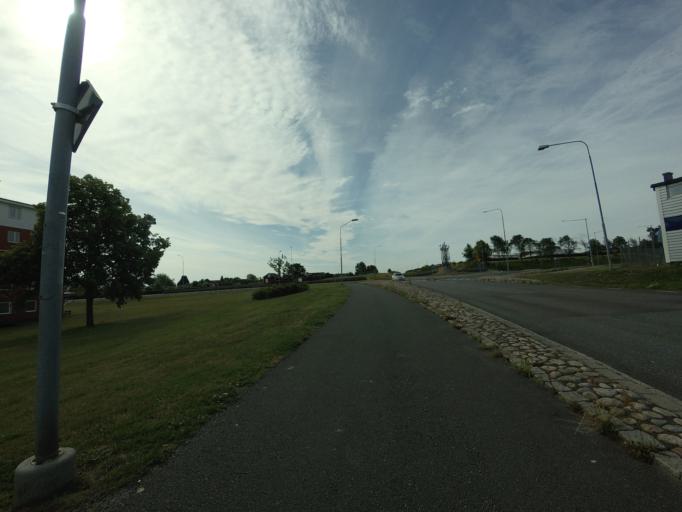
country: SE
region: Skane
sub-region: Simrishamns Kommun
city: Simrishamn
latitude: 55.5505
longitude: 14.3492
